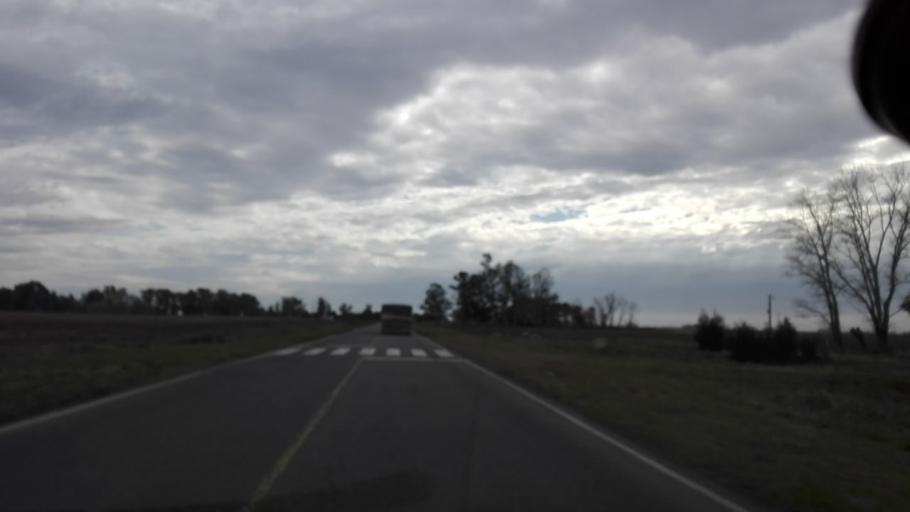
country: AR
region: Buenos Aires
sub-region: Partido de Las Flores
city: Las Flores
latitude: -36.2127
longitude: -59.0460
